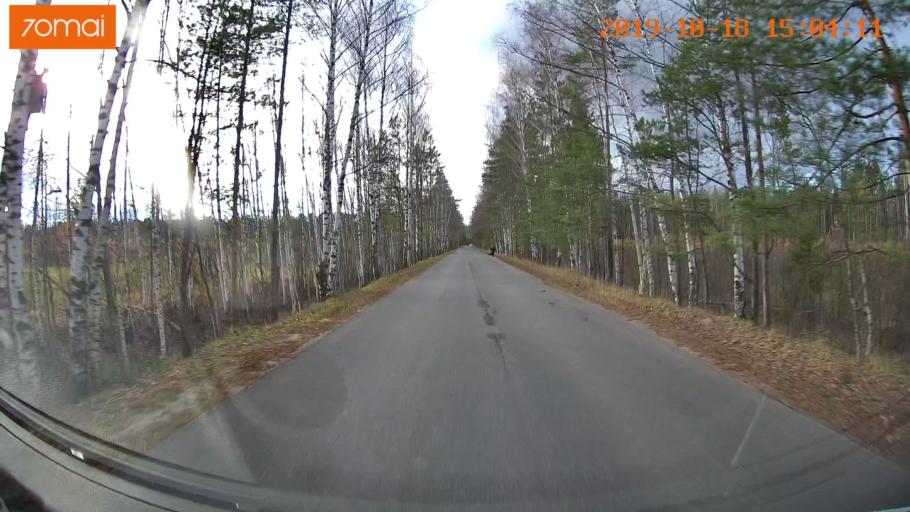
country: RU
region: Vladimir
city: Kurlovo
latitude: 55.5041
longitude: 40.5785
